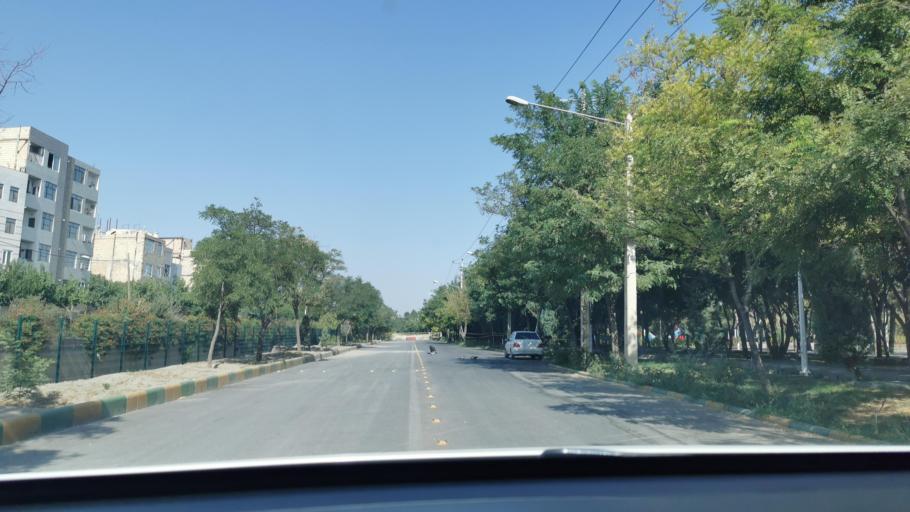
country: IR
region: Razavi Khorasan
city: Mashhad
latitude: 36.3303
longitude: 59.6334
